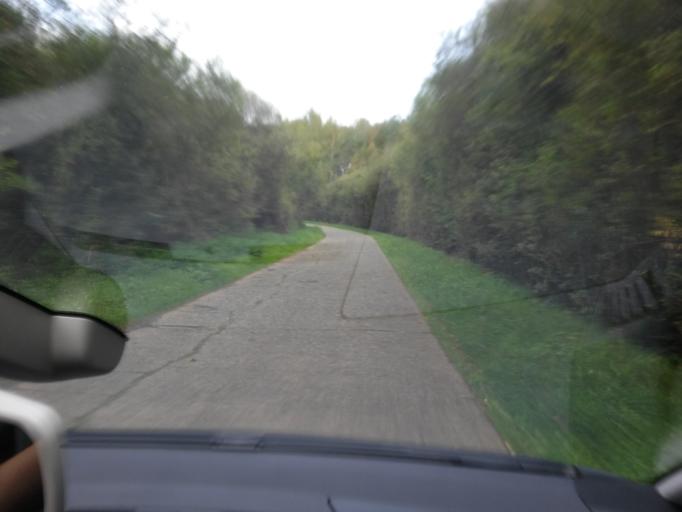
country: BE
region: Wallonia
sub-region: Province du Luxembourg
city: Arlon
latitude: 49.6769
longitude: 5.7725
